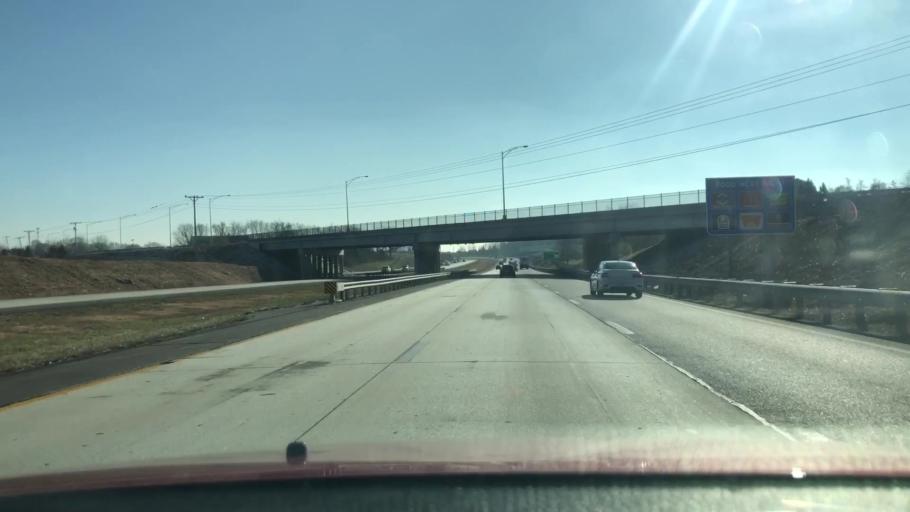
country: US
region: Missouri
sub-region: Greene County
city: Battlefield
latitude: 37.1389
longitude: -93.3121
